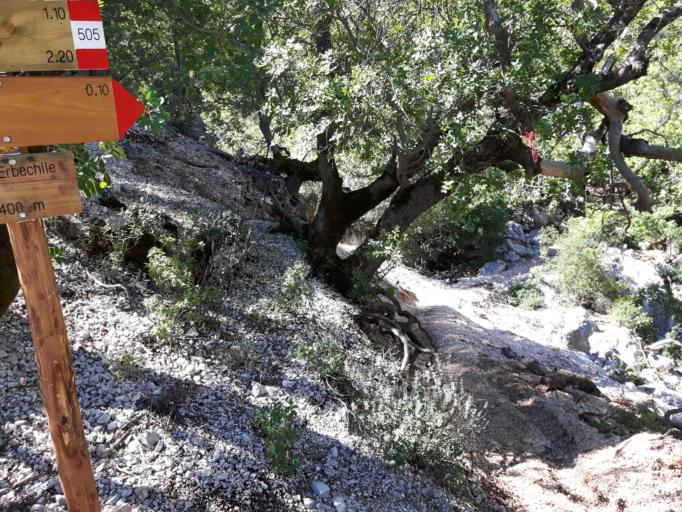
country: IT
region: Sardinia
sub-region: Provincia di Ogliastra
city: Urzulei
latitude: 40.1844
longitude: 9.5039
